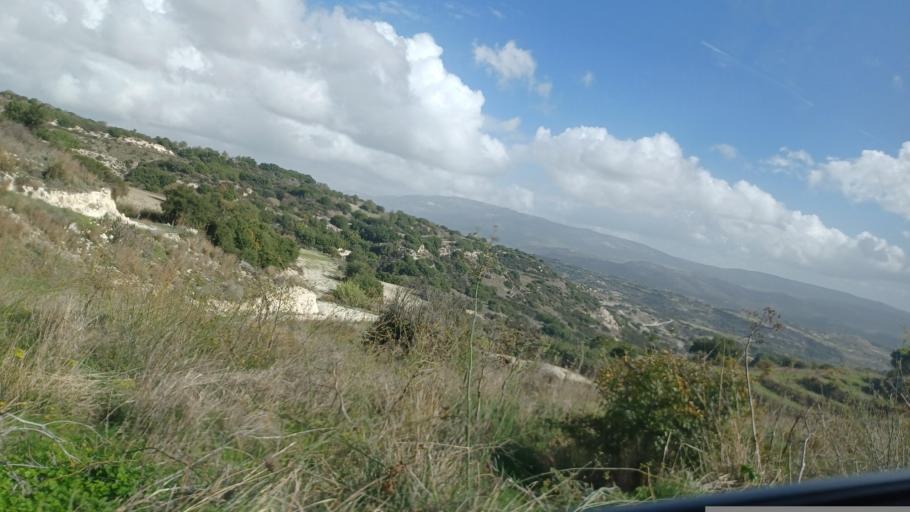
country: CY
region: Pafos
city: Mesogi
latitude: 34.8768
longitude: 32.5141
